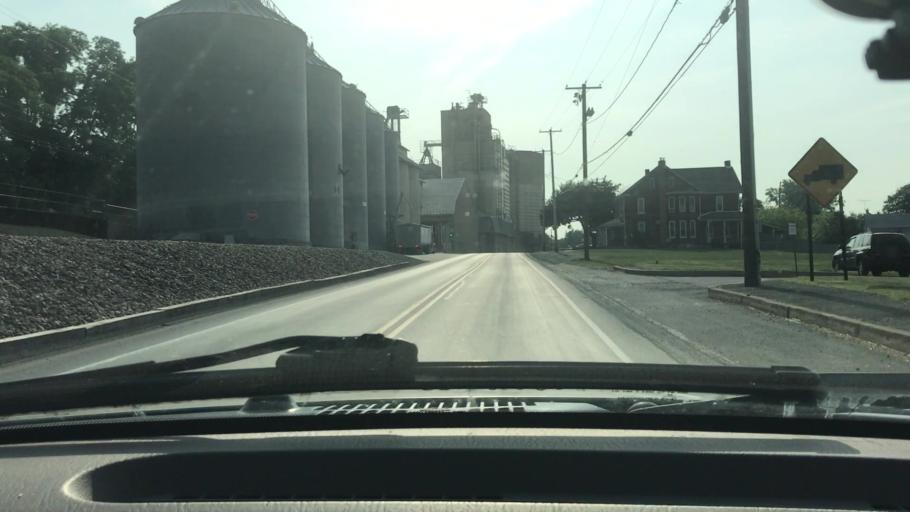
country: US
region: Pennsylvania
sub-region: Lancaster County
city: Rheems
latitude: 40.1312
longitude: -76.5742
